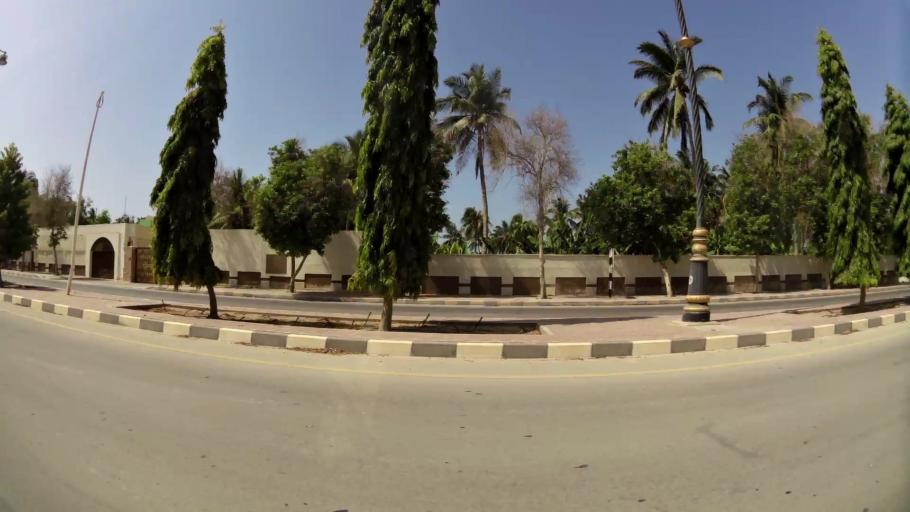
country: OM
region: Zufar
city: Salalah
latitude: 17.0262
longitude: 54.1540
